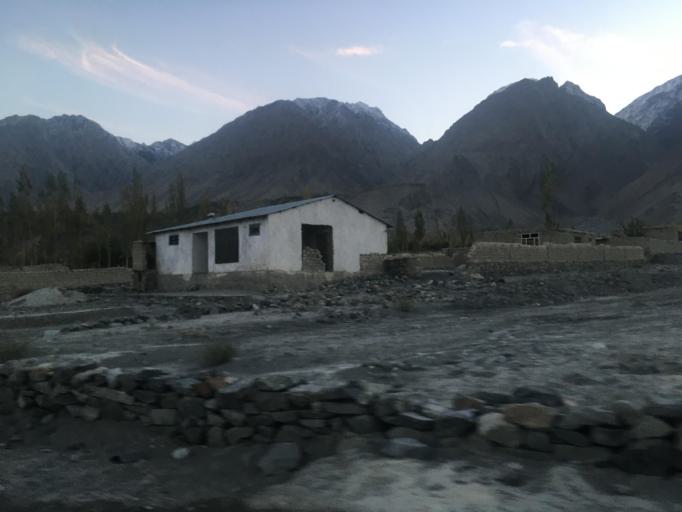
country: PK
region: Gilgit-Baltistan
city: Skardu
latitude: 35.3007
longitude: 75.5428
